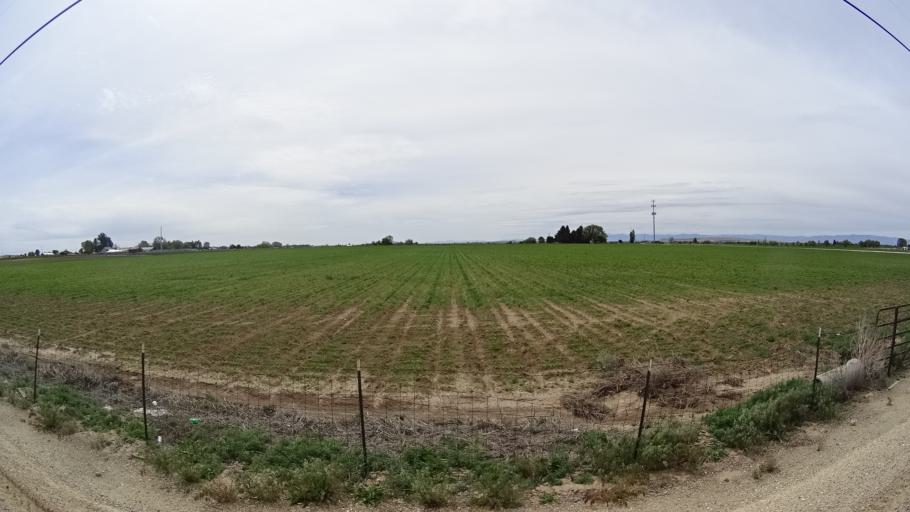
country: US
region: Idaho
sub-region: Ada County
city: Kuna
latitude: 43.5320
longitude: -116.3597
